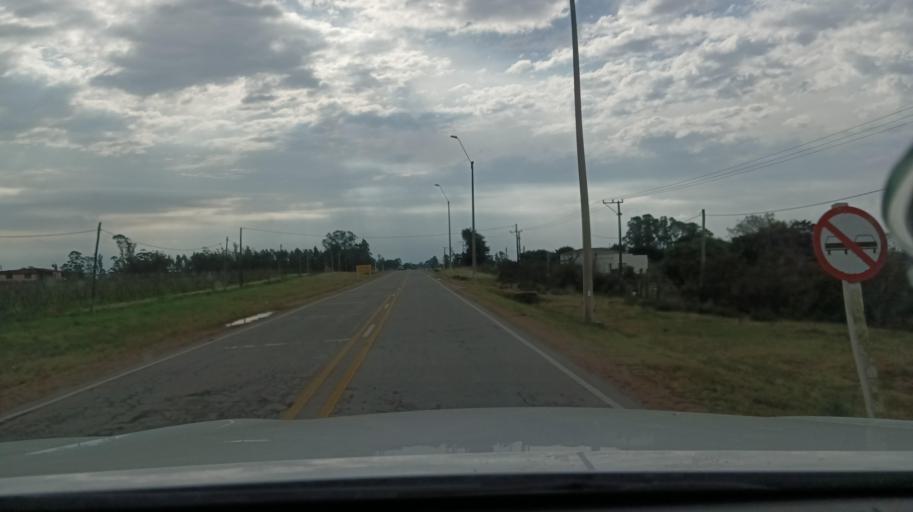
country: UY
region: Canelones
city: Toledo
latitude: -34.7010
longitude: -56.1052
